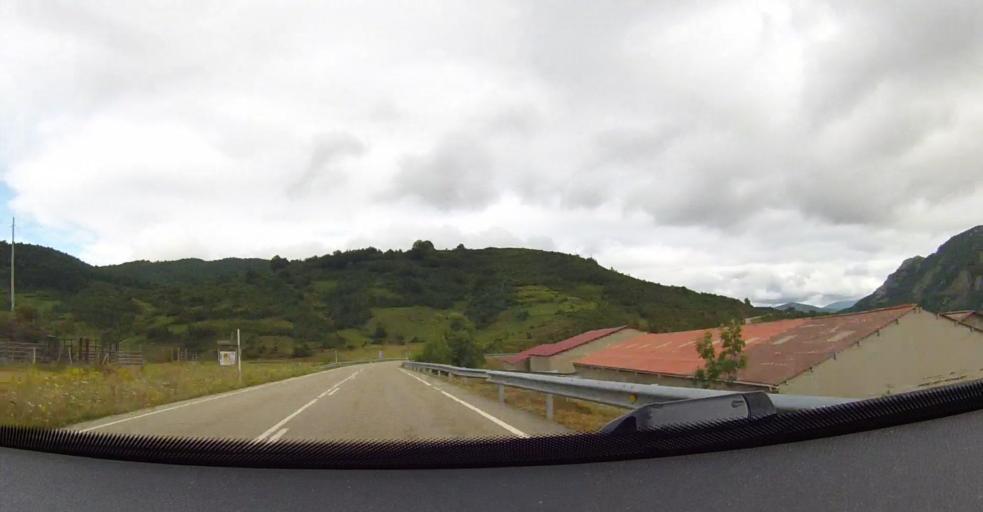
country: ES
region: Castille and Leon
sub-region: Provincia de Leon
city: Buron
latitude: 43.0259
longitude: -5.0491
